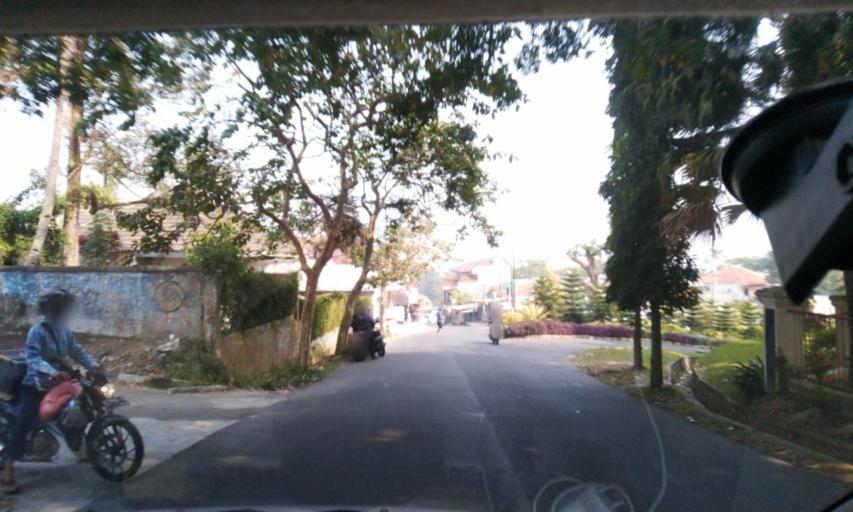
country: ID
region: West Java
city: Caringin
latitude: -6.6618
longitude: 106.8589
